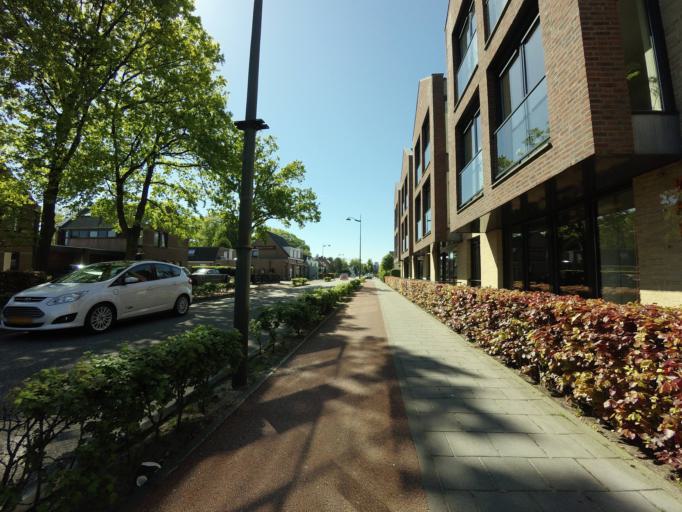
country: NL
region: North Brabant
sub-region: Gemeente Rucphen
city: Rucphen
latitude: 51.5600
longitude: 4.5447
